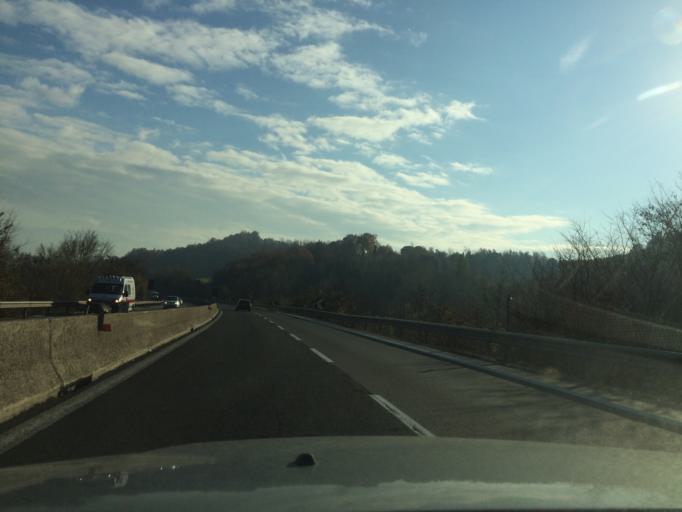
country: IT
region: Umbria
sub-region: Provincia di Terni
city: San Gemini
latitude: 42.6088
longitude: 12.5557
